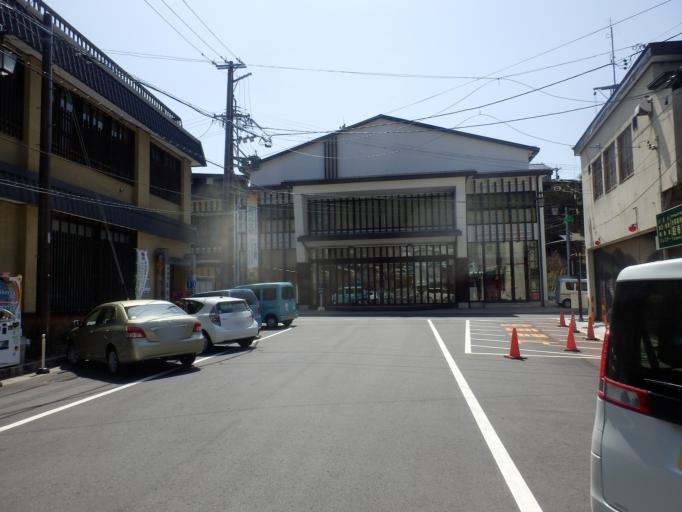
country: JP
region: Nagano
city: Ina
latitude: 35.8501
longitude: 137.6985
